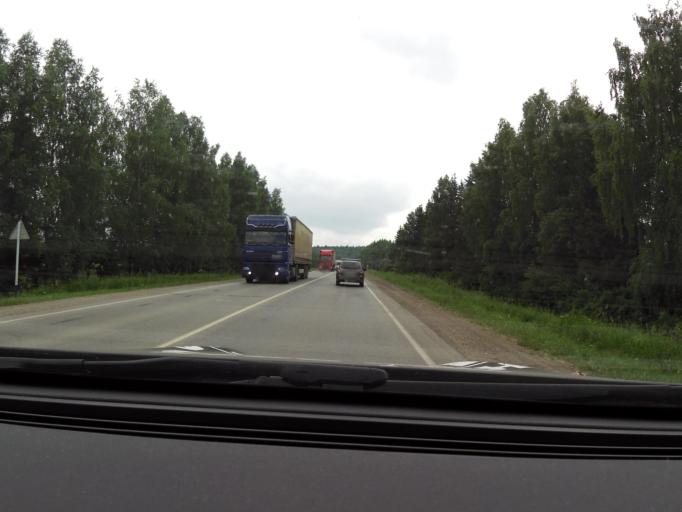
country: RU
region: Perm
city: Kukushtan
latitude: 57.4892
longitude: 56.6663
